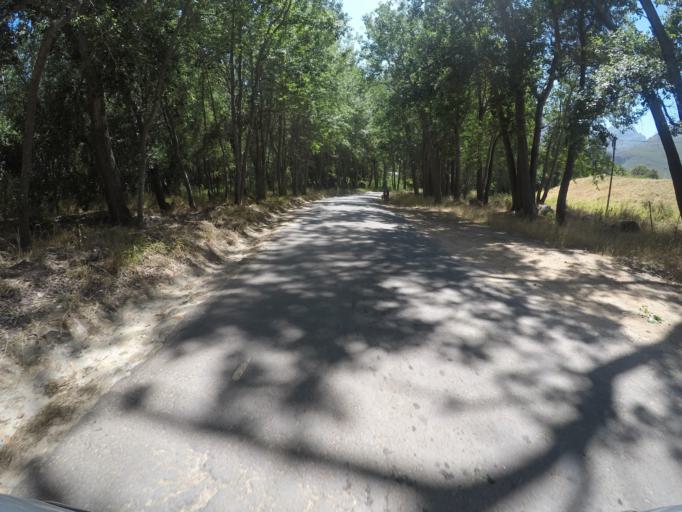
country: ZA
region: Western Cape
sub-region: Cape Winelands District Municipality
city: Stellenbosch
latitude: -33.9957
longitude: 18.8763
